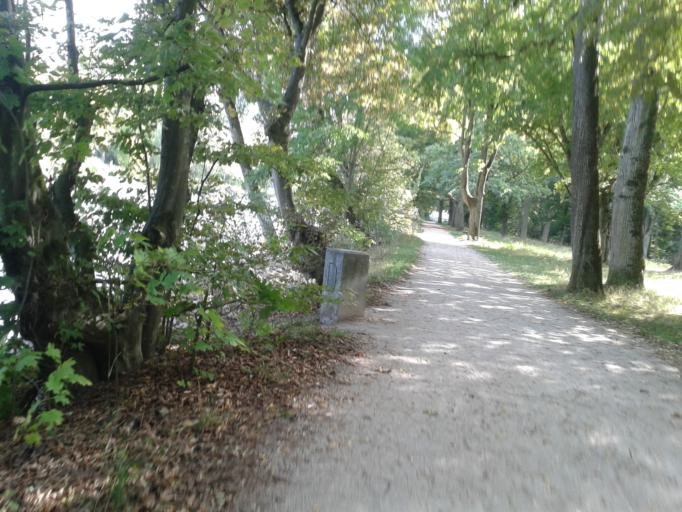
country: DE
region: Bavaria
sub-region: Upper Franconia
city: Bamberg
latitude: 49.8754
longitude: 10.9053
